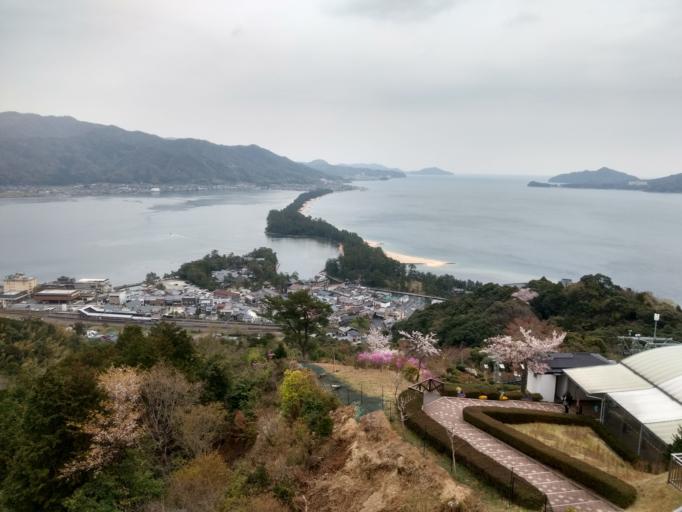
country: JP
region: Kyoto
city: Miyazu
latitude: 35.5527
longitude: 135.1818
